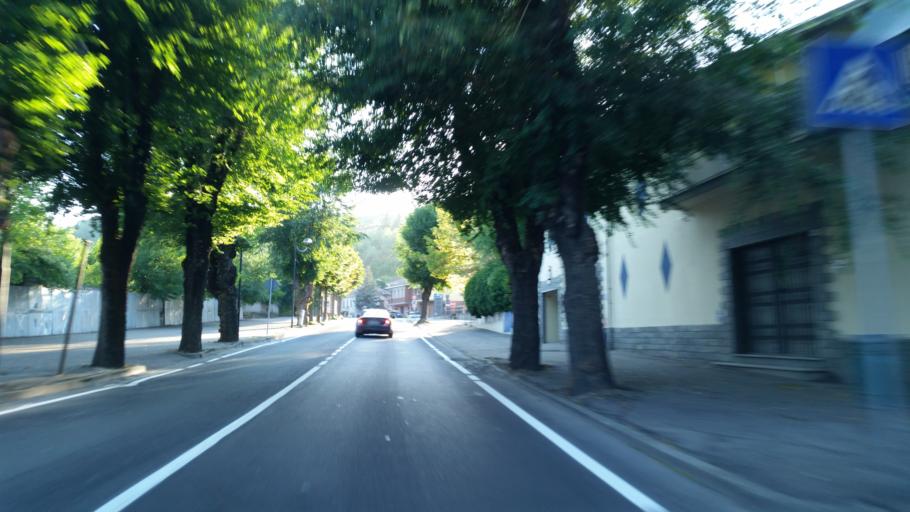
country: IT
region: Piedmont
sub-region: Provincia di Asti
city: Canelli
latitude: 44.7180
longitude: 8.2750
